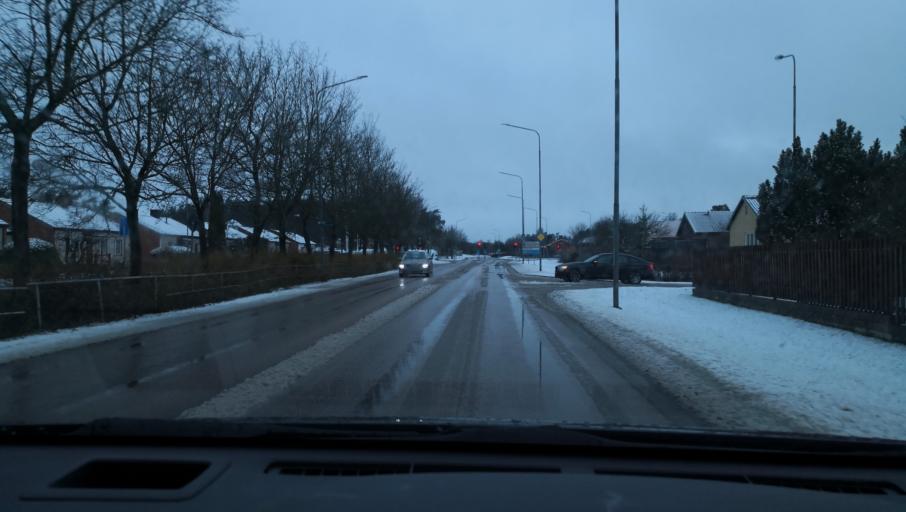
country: SE
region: Vaestmanland
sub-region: Kopings Kommun
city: Koping
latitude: 59.5189
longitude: 16.0079
